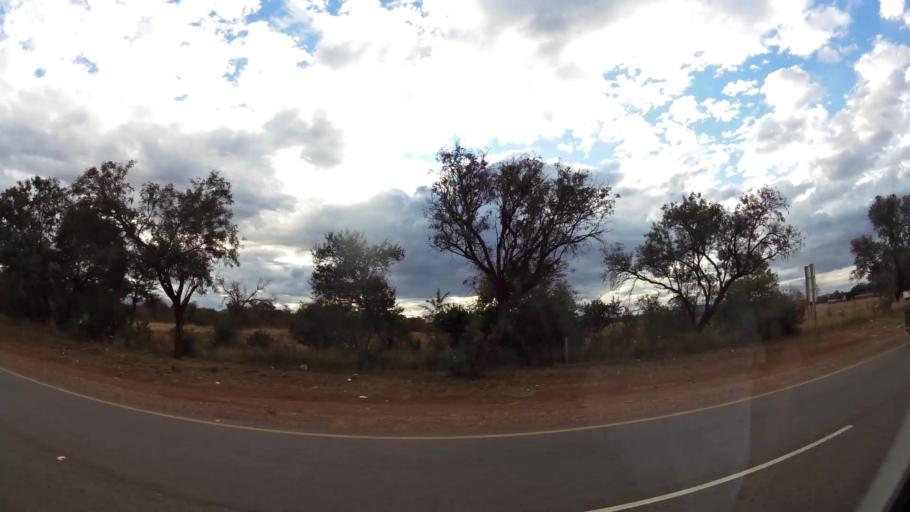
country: ZA
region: Limpopo
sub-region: Waterberg District Municipality
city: Modimolle
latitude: -24.5028
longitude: 28.7306
